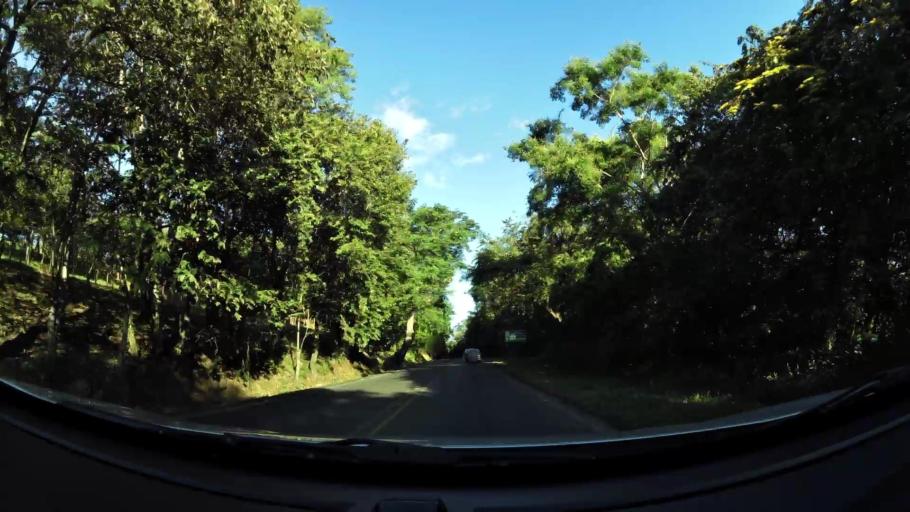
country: CR
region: Puntarenas
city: Miramar
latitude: 10.0921
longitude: -84.7972
